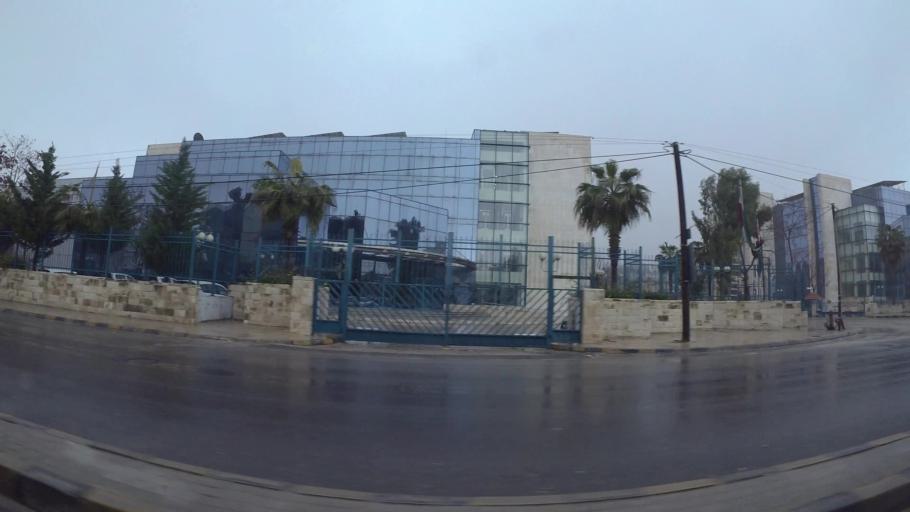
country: JO
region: Amman
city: Al Jubayhah
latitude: 32.0070
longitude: 35.8336
